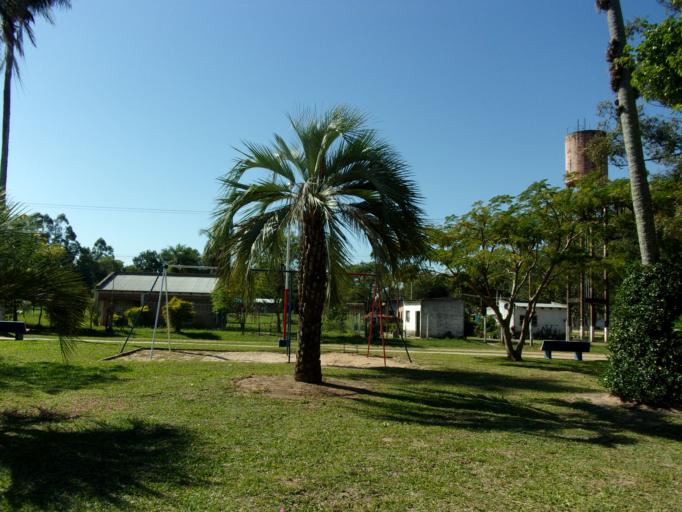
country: AR
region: Corrientes
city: Yataity Calle
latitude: -29.0283
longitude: -58.9122
